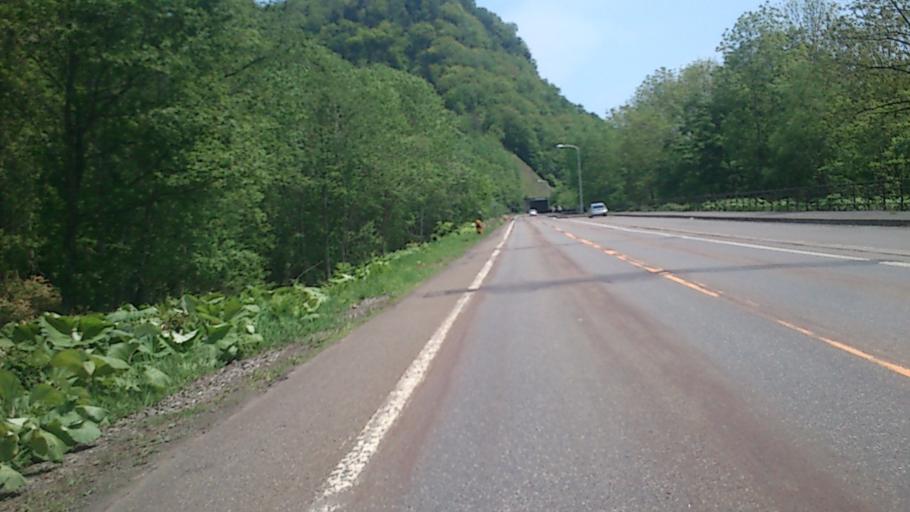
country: JP
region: Hokkaido
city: Otofuke
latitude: 43.3560
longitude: 143.2566
